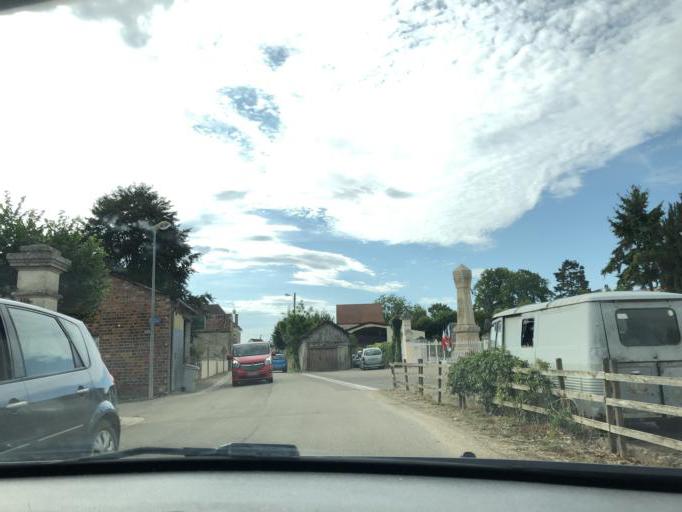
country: FR
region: Bourgogne
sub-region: Departement de l'Yonne
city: Chablis
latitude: 47.7917
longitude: 3.8327
